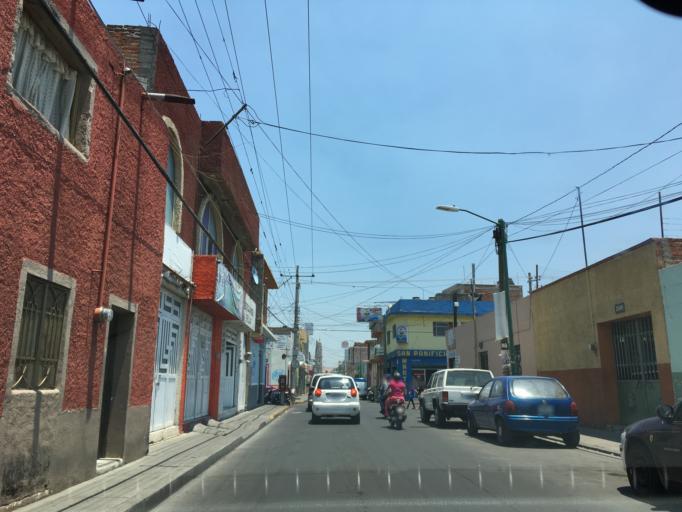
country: MX
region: Guanajuato
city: Uriangato
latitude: 20.1376
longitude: -101.1787
